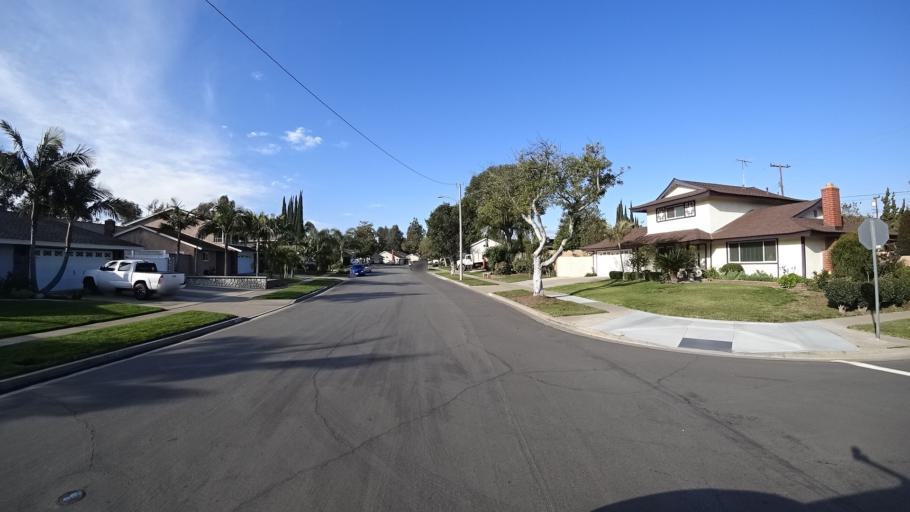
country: US
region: California
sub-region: Orange County
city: Yorba Linda
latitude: 33.8535
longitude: -117.8127
